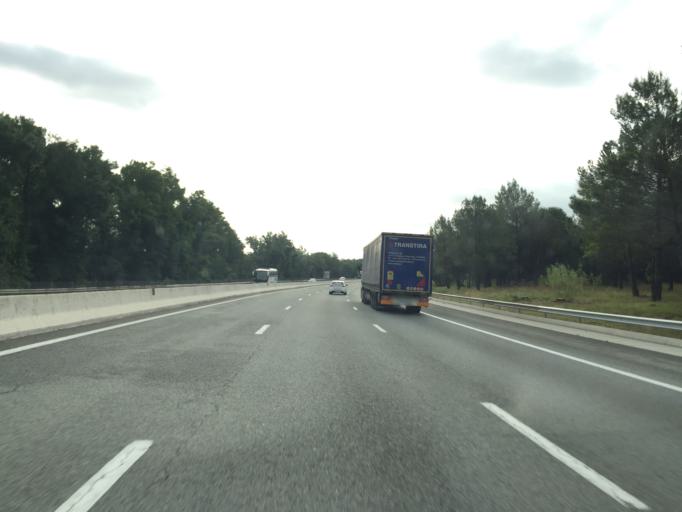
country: FR
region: Provence-Alpes-Cote d'Azur
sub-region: Departement du Var
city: La Motte
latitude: 43.4559
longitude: 6.5296
